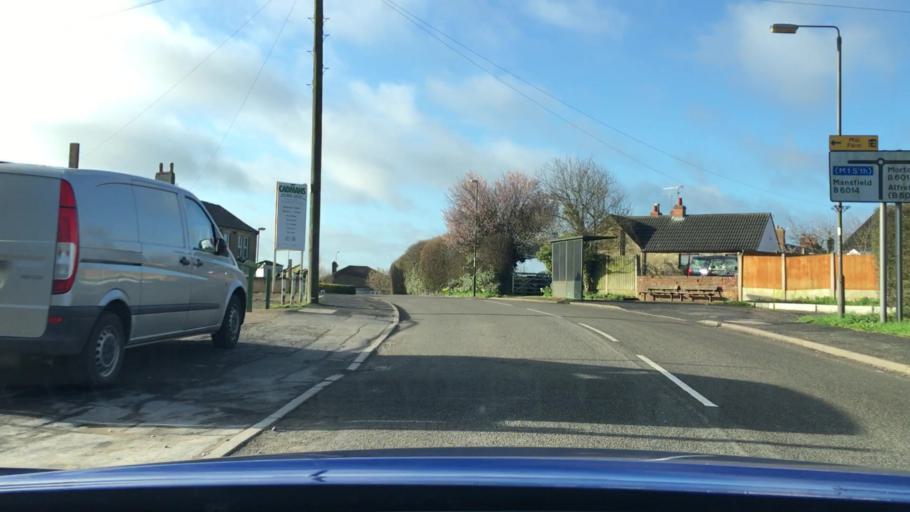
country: GB
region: England
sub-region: Derbyshire
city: Tibshelf
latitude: 53.1480
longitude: -1.3359
